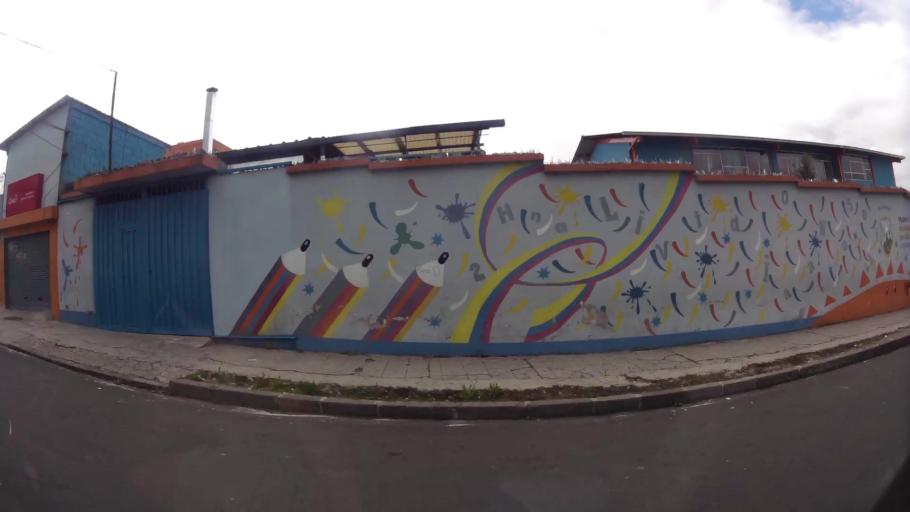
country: EC
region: Pichincha
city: Quito
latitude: -0.1392
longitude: -78.4958
